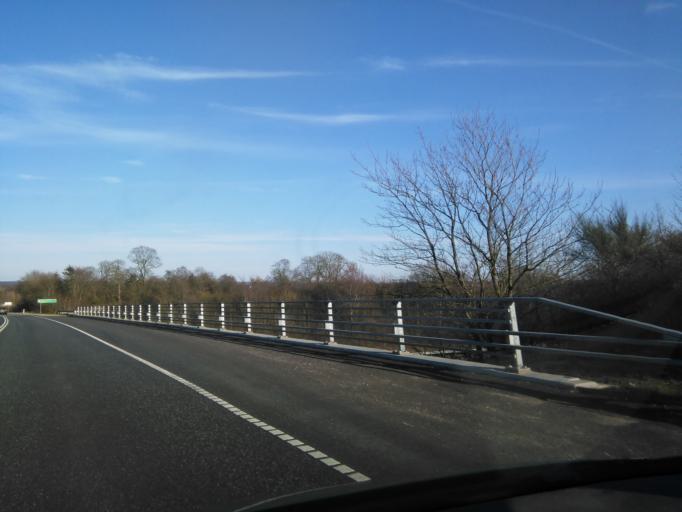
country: DK
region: Central Jutland
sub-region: Skanderborg Kommune
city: Skanderborg
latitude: 56.0289
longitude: 9.8812
